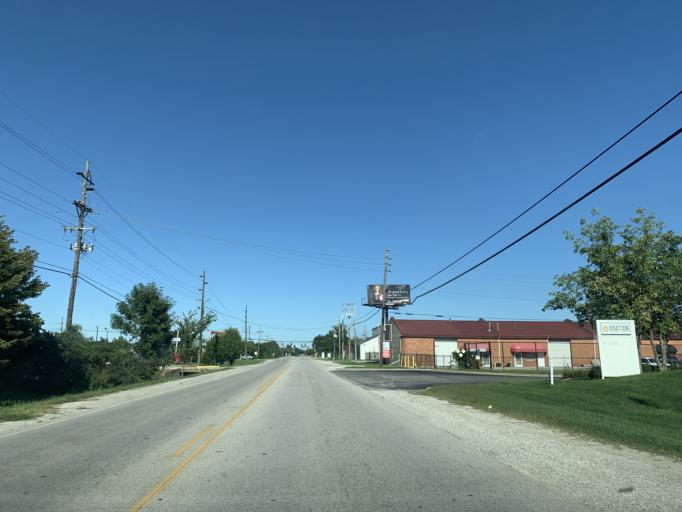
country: US
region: Kentucky
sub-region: Jefferson County
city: West Buechel
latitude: 38.1835
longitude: -85.6842
